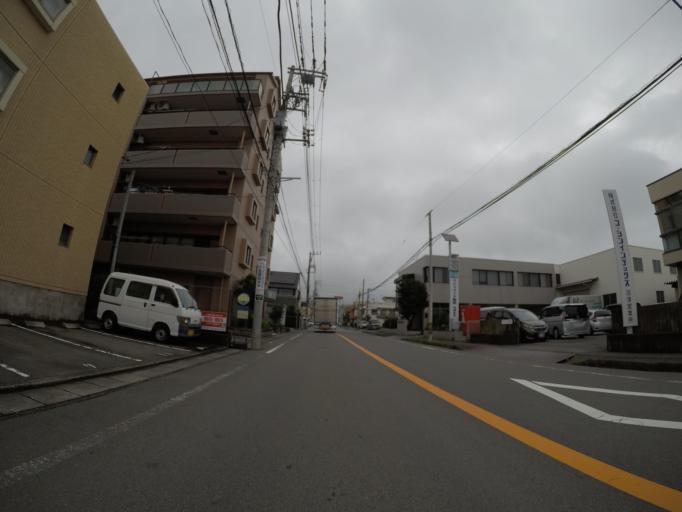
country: JP
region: Shizuoka
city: Numazu
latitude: 35.1184
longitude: 138.8531
